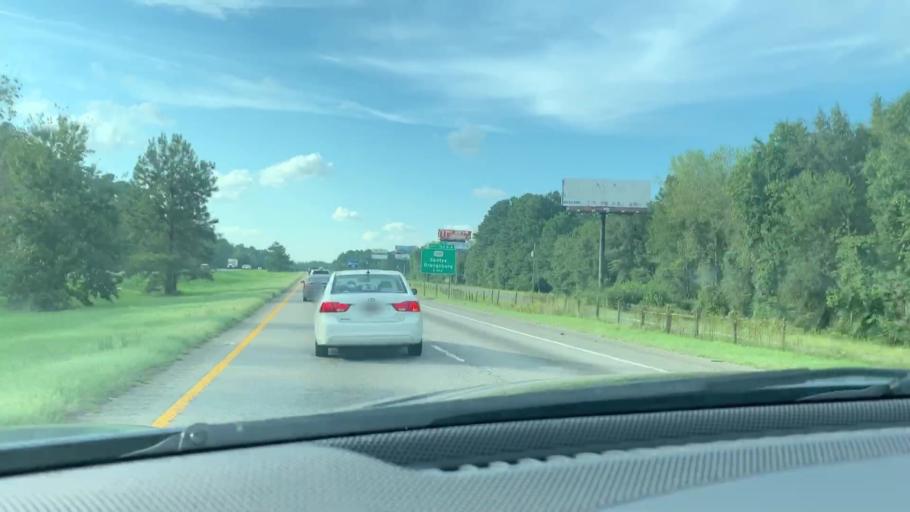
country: US
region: South Carolina
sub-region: Orangeburg County
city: Brookdale
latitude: 33.4461
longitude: -80.7146
